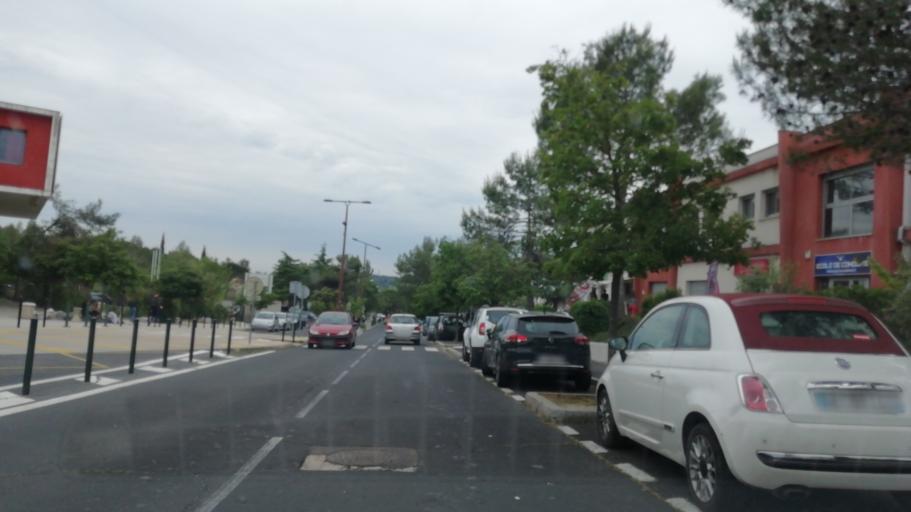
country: FR
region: Languedoc-Roussillon
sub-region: Departement de l'Herault
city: Les Matelles
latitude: 43.7113
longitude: 3.8335
